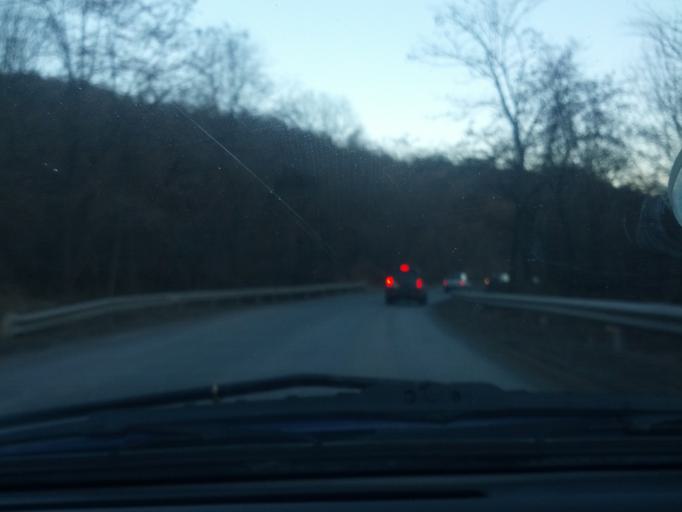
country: BG
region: Vratsa
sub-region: Obshtina Mezdra
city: Mezdra
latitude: 43.0206
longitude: 23.6840
